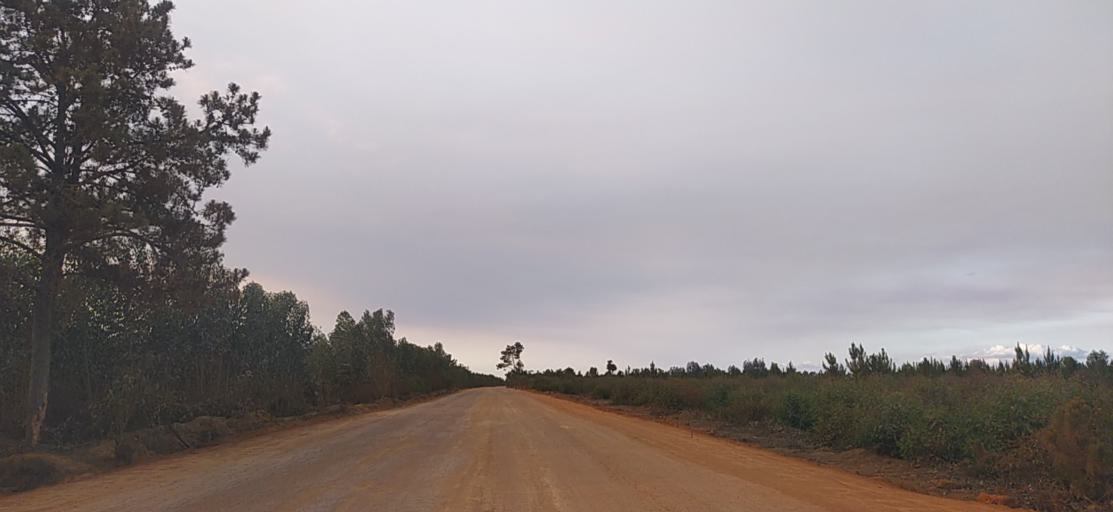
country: MG
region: Analamanga
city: Anjozorobe
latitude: -18.4720
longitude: 48.2618
